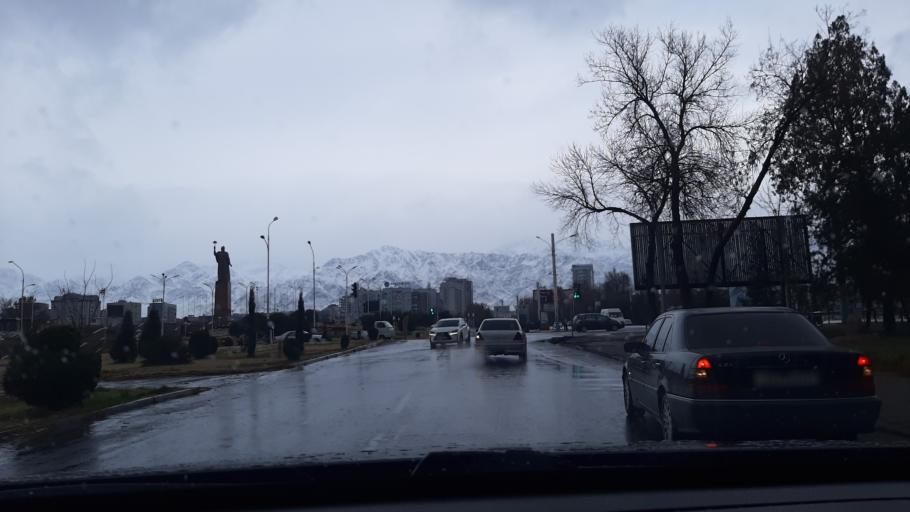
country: TJ
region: Viloyati Sughd
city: Khujand
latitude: 40.2937
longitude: 69.6177
